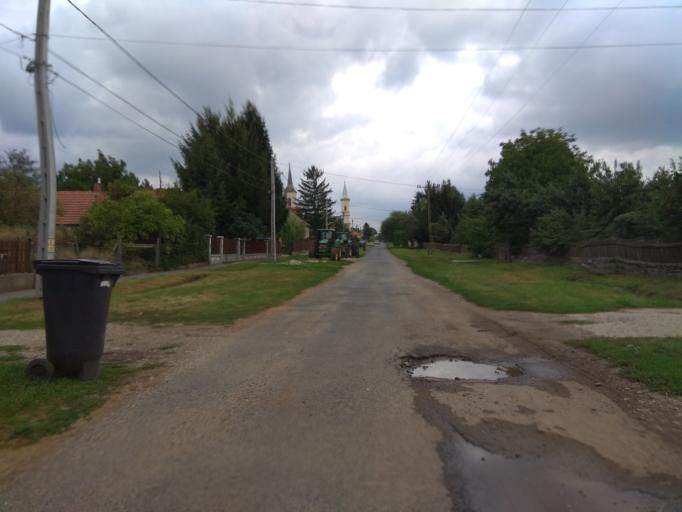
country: HU
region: Borsod-Abauj-Zemplen
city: Gesztely
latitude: 48.1360
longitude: 21.0046
